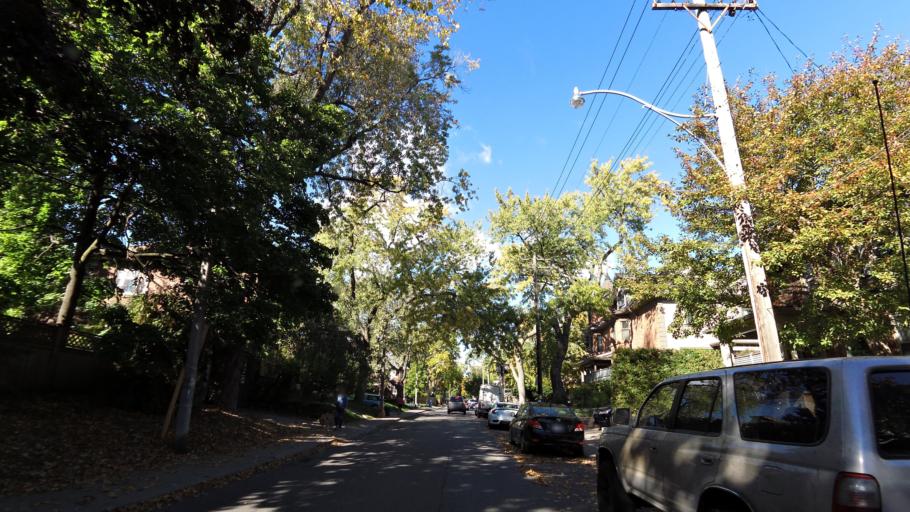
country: CA
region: Ontario
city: Toronto
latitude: 43.6452
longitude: -79.4511
